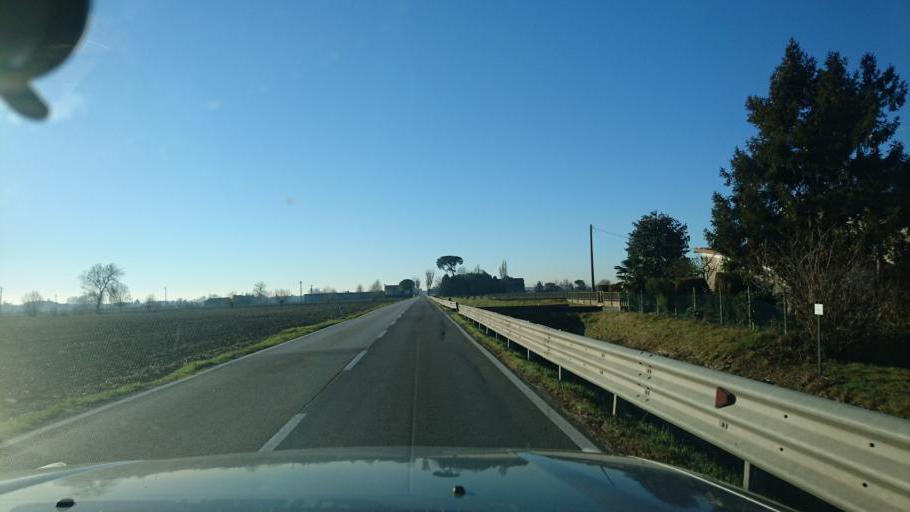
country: IT
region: Veneto
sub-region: Provincia di Venezia
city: Pegolotte
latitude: 45.2064
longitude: 12.0392
